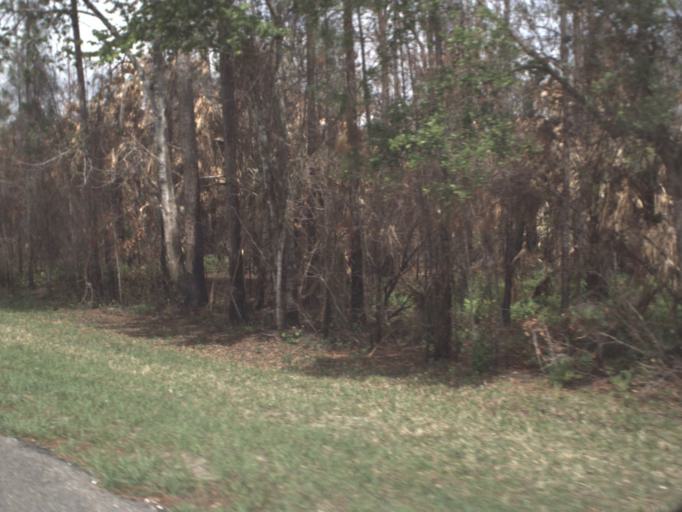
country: US
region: Florida
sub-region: Flagler County
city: Bunnell
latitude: 29.3801
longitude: -81.3103
